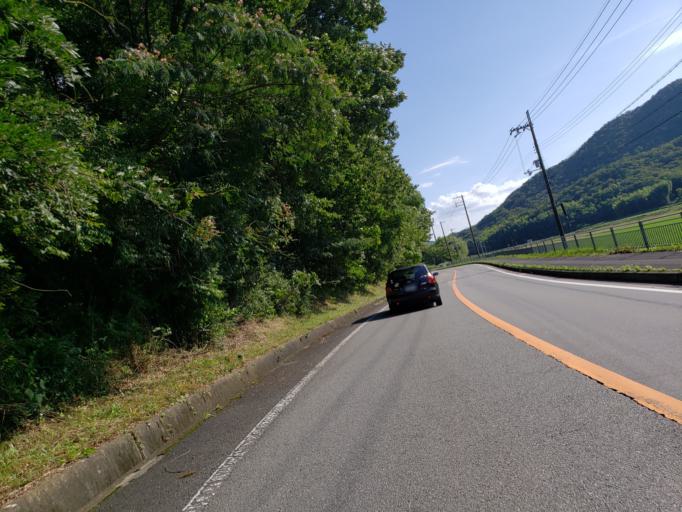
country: JP
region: Hyogo
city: Kakogawacho-honmachi
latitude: 34.8715
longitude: 134.7959
